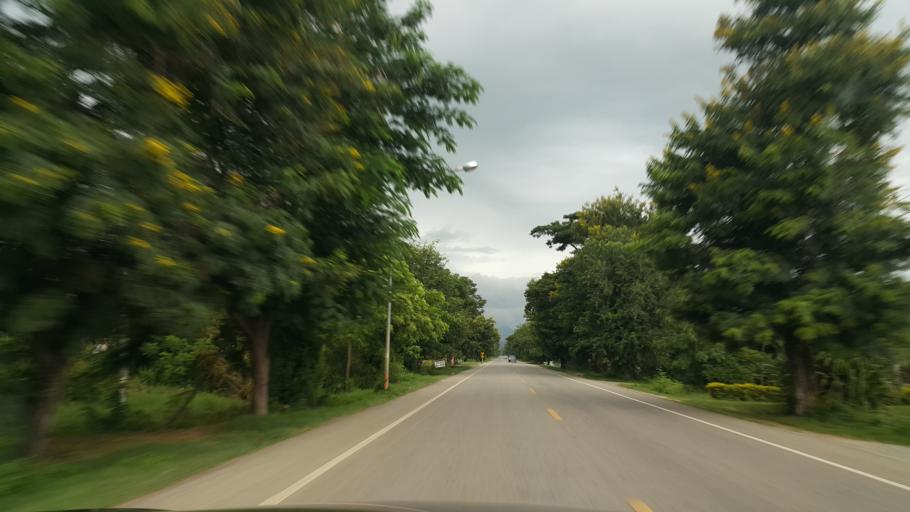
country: TH
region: Phayao
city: Dok Kham Tai
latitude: 19.2033
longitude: 100.0333
